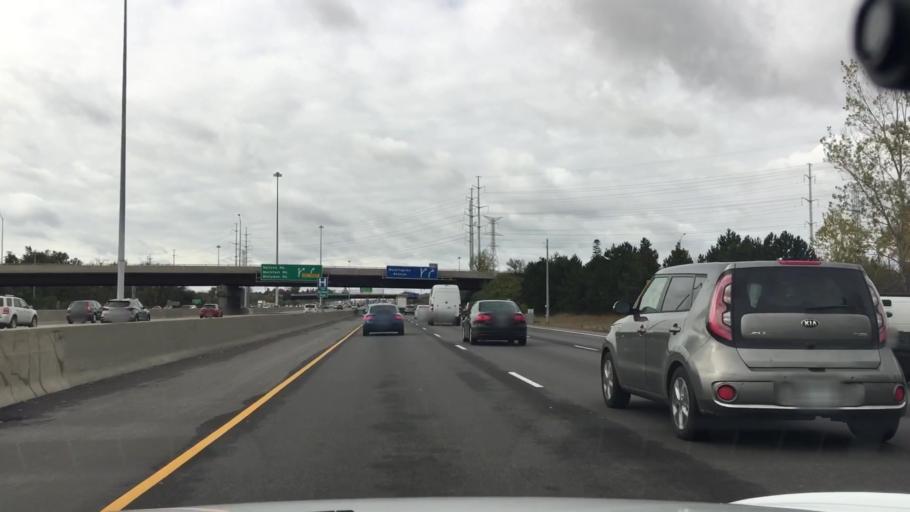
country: CA
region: Ontario
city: Scarborough
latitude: 43.7985
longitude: -79.1857
